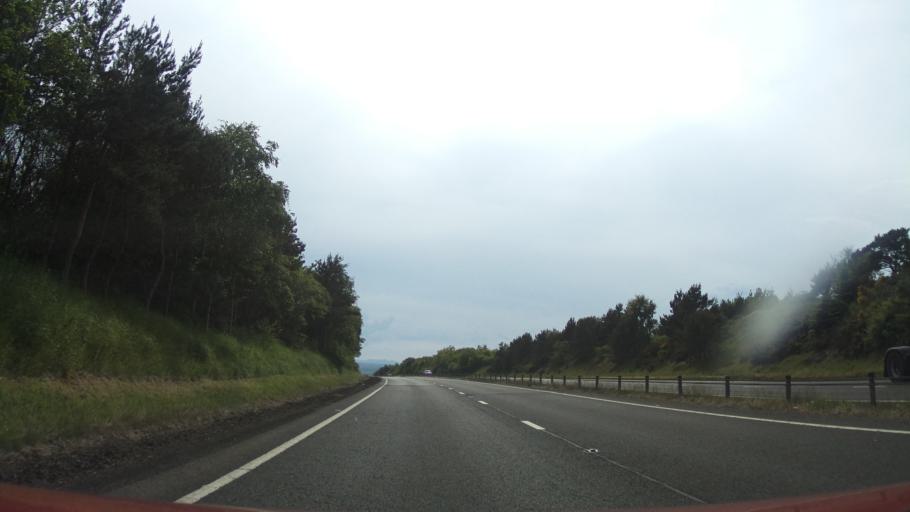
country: GB
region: Scotland
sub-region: East Lothian
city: East Linton
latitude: 55.9794
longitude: -2.6899
